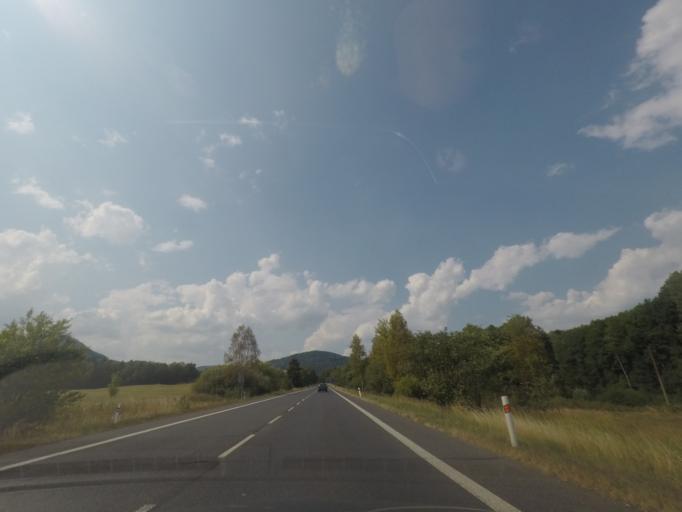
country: CZ
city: Cvikov
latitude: 50.7860
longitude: 14.6118
